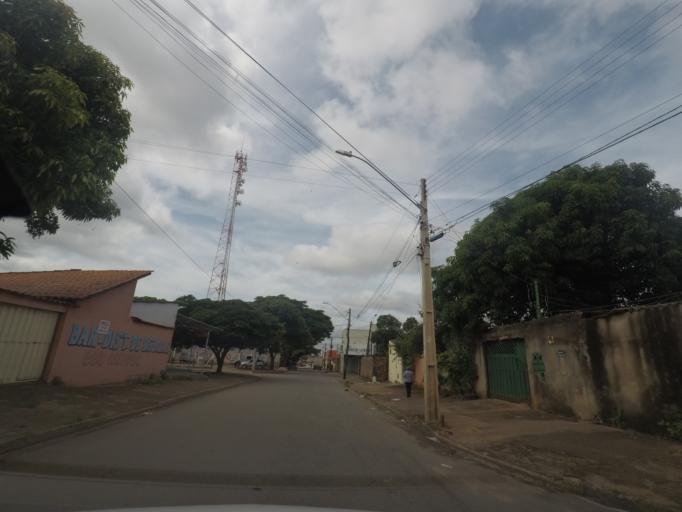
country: BR
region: Goias
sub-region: Goiania
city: Goiania
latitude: -16.6653
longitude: -49.1852
